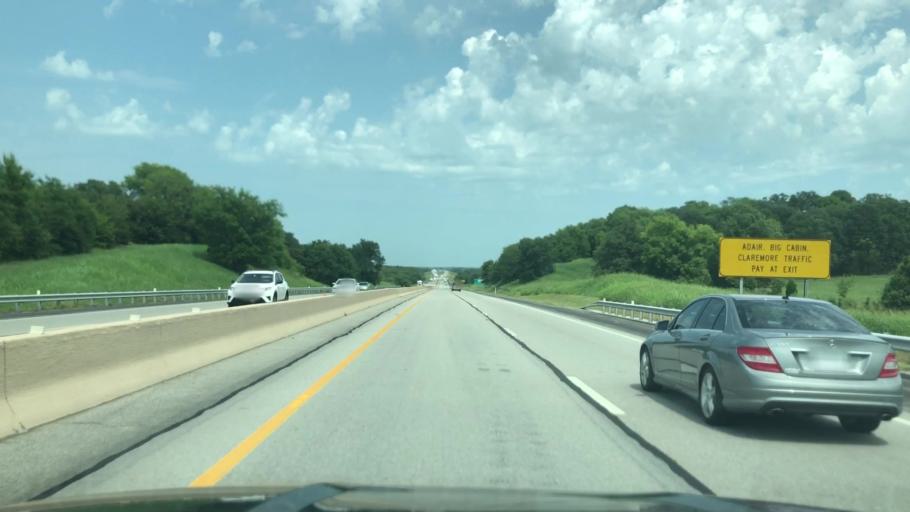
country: US
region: Oklahoma
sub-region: Rogers County
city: Catoosa
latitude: 36.1896
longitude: -95.7248
